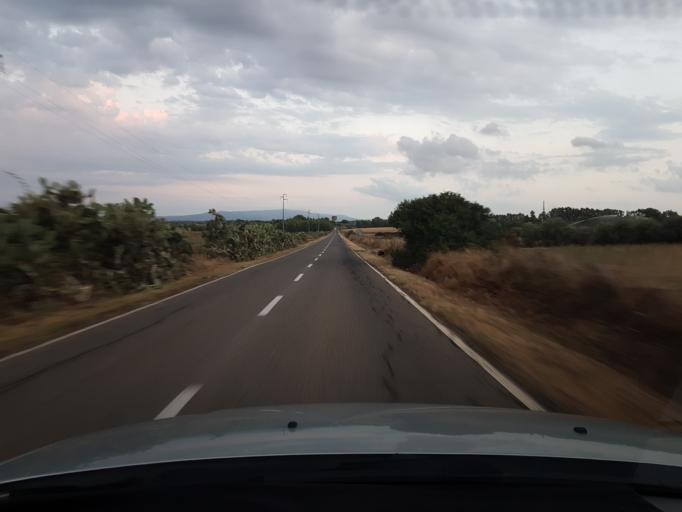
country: IT
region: Sardinia
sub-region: Provincia di Oristano
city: Tramatza
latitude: 40.0168
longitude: 8.6438
